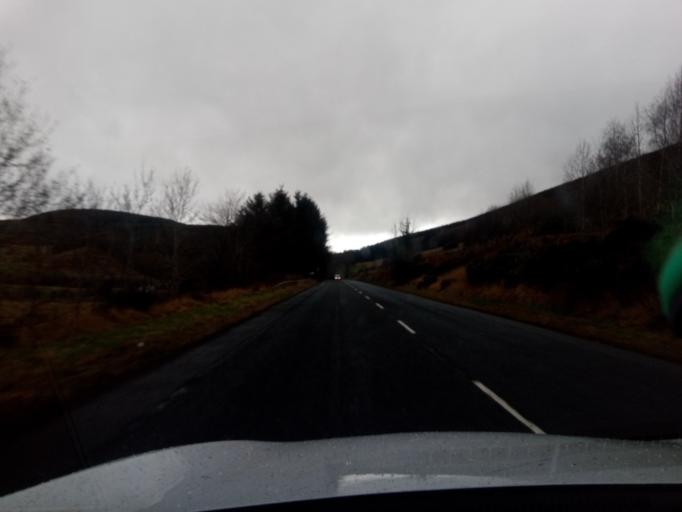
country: GB
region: Scotland
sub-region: The Scottish Borders
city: Innerleithen
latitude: 55.6282
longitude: -3.0005
